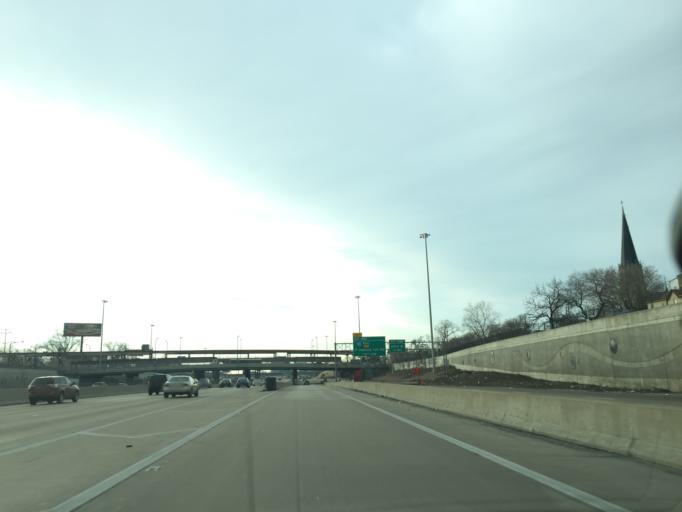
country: US
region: Illinois
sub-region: Cook County
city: Chicago
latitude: 41.7897
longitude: -87.6314
